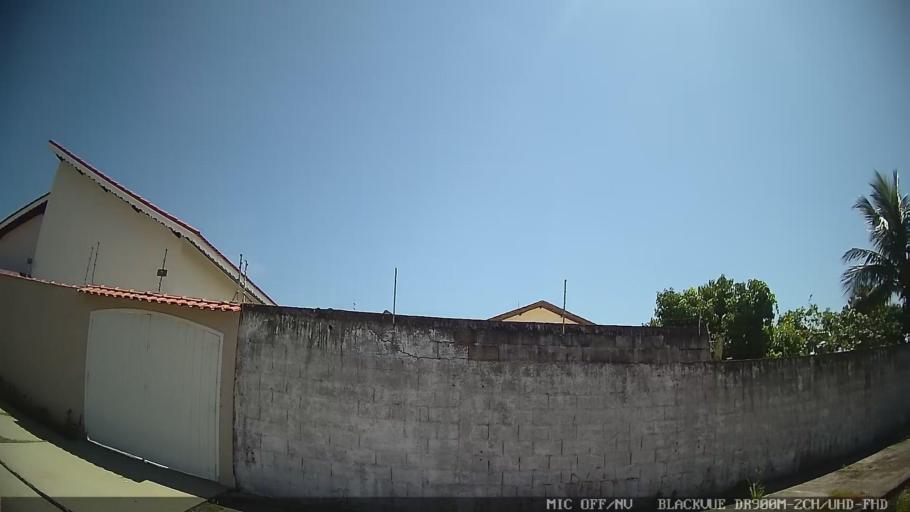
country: BR
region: Sao Paulo
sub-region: Peruibe
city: Peruibe
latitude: -24.2898
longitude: -46.9676
